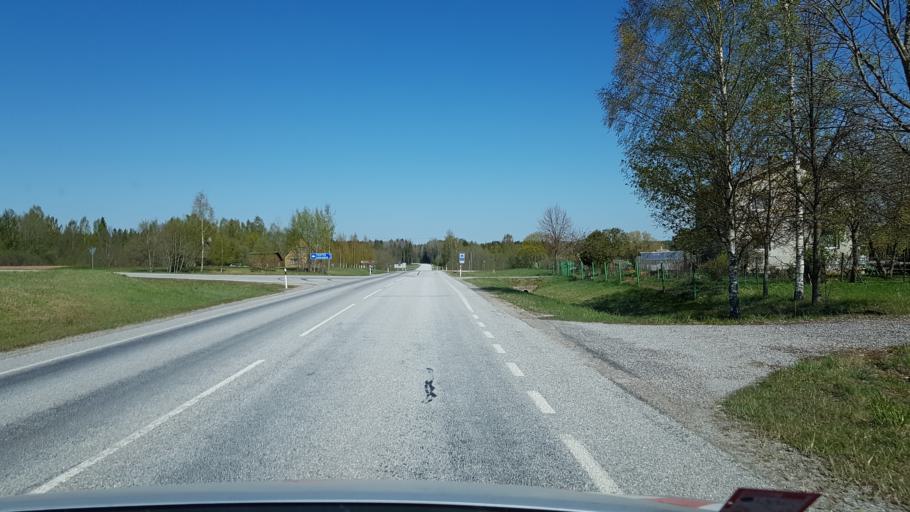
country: RU
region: Pskov
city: Pechory
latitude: 57.7125
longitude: 27.3203
